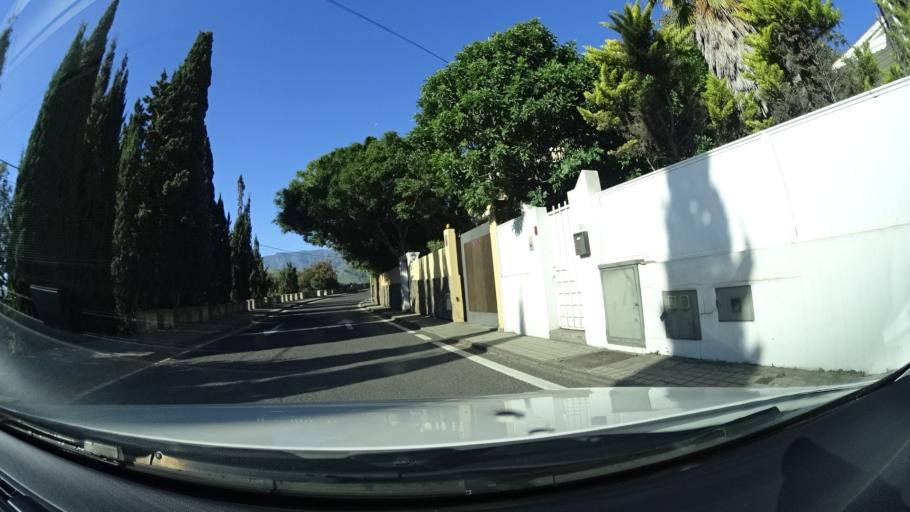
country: ES
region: Canary Islands
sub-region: Provincia de Las Palmas
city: Santa Brigida
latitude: 28.0307
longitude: -15.4682
